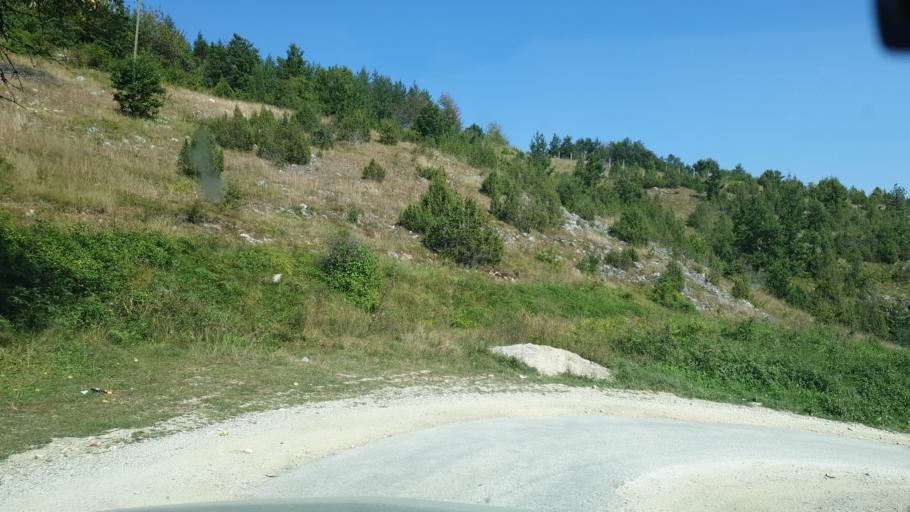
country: RS
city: Zlatibor
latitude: 43.6544
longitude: 19.8298
